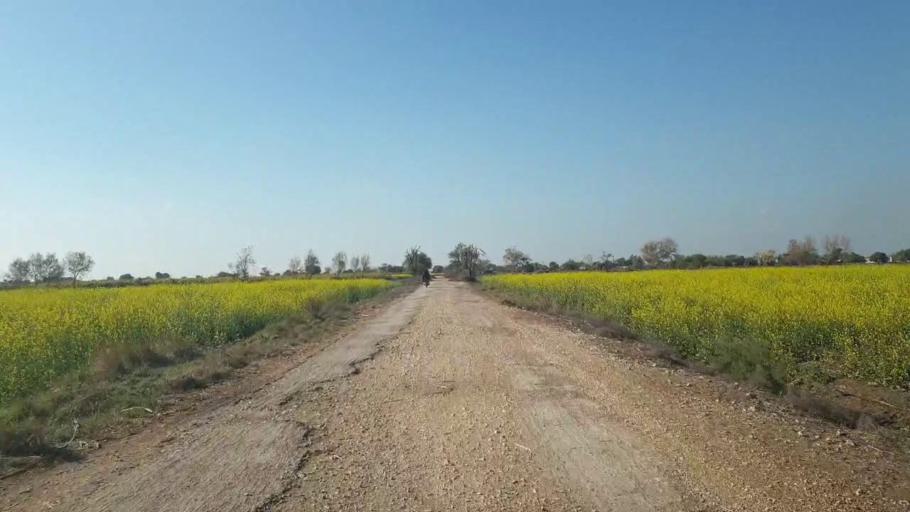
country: PK
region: Sindh
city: Shahdadpur
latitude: 25.9310
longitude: 68.5274
